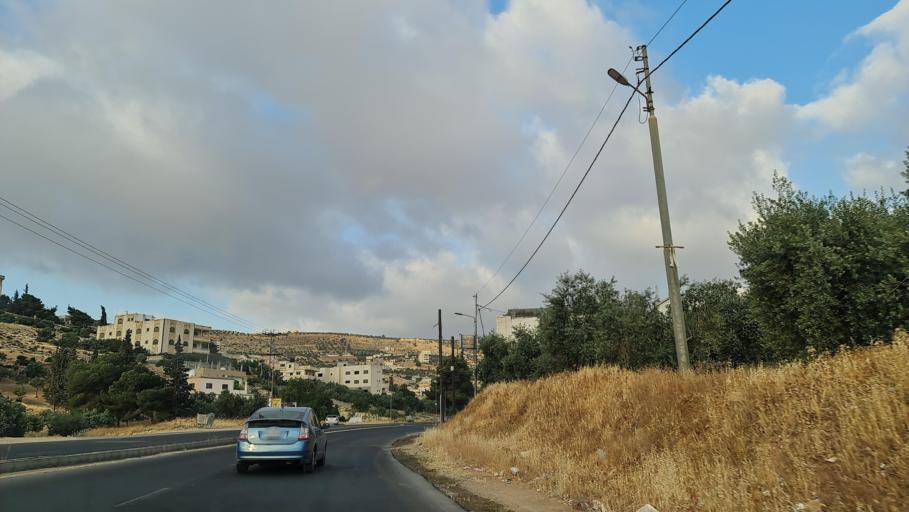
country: JO
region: Amman
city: Al Jubayhah
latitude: 32.0940
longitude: 35.9541
